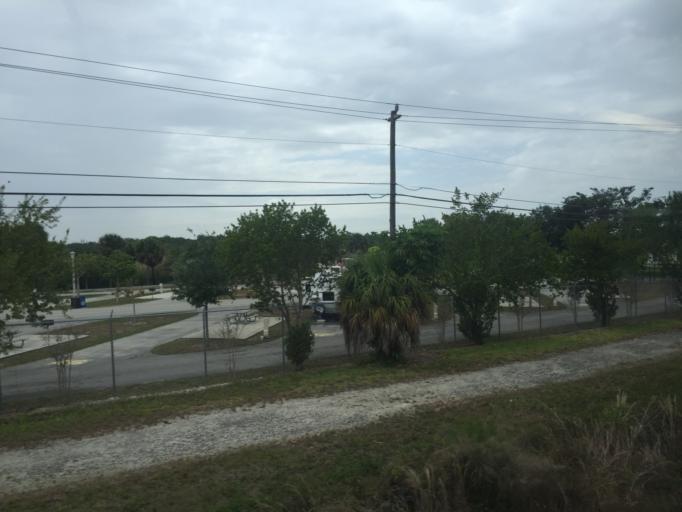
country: US
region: Florida
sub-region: Broward County
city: Dania Beach
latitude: 26.0360
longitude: -80.1683
